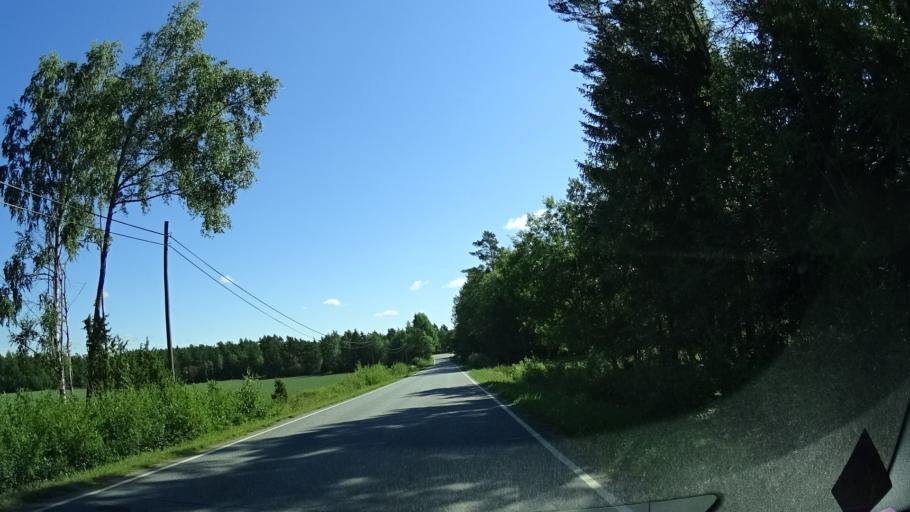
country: FI
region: Varsinais-Suomi
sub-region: Turku
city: Velkua
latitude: 60.5114
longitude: 21.7409
